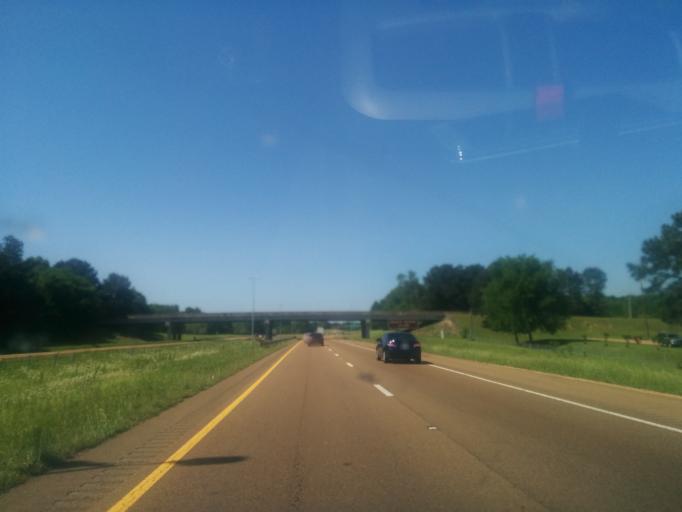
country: US
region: Mississippi
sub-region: Hinds County
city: Jackson
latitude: 32.3182
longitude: -90.2473
